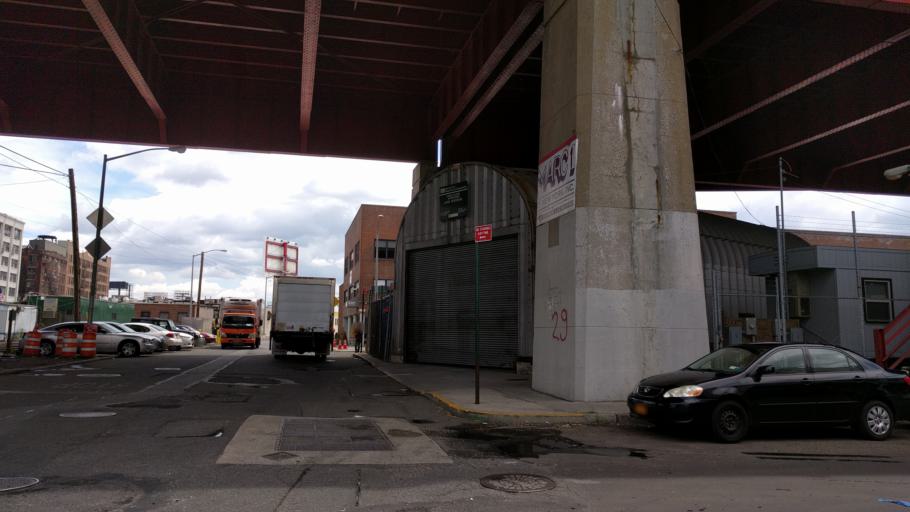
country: US
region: New York
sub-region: Queens County
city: Long Island City
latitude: 40.7404
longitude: -73.9525
